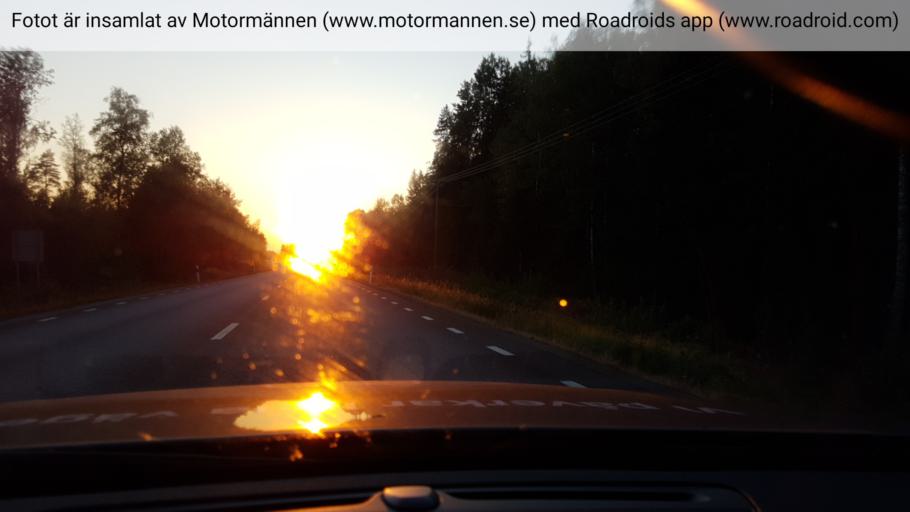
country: SE
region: Uppsala
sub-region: Osthammars Kommun
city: Bjorklinge
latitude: 59.9671
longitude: 17.3798
